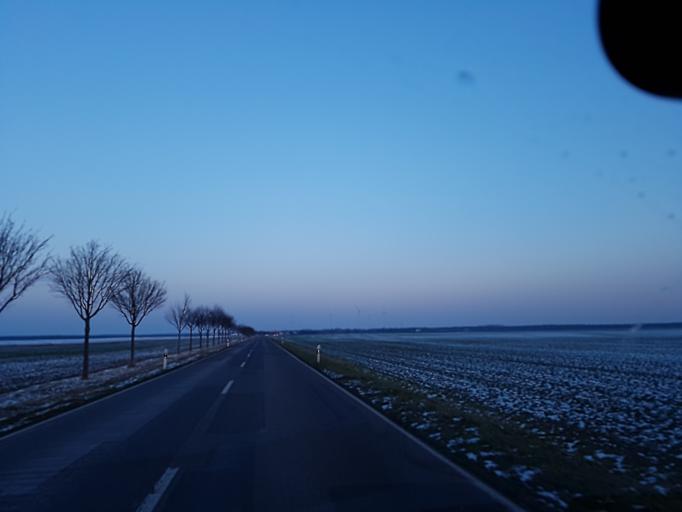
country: DE
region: Brandenburg
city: Muhlberg
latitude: 51.4641
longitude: 13.2718
